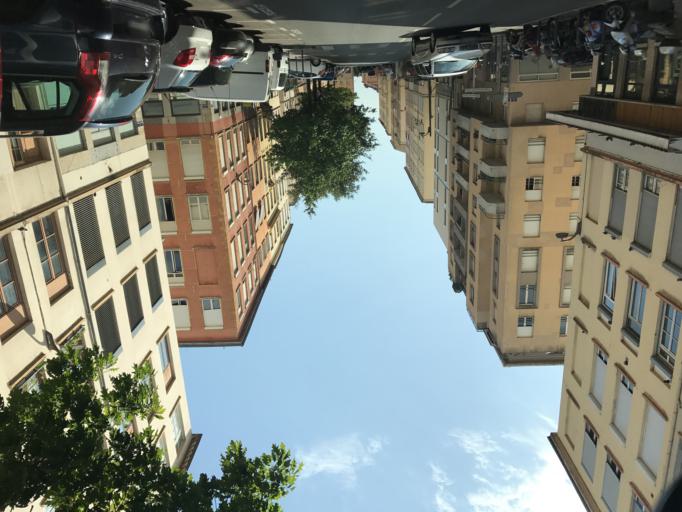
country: FR
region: Rhone-Alpes
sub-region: Departement du Rhone
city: Caluire-et-Cuire
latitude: 45.7789
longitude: 4.8362
